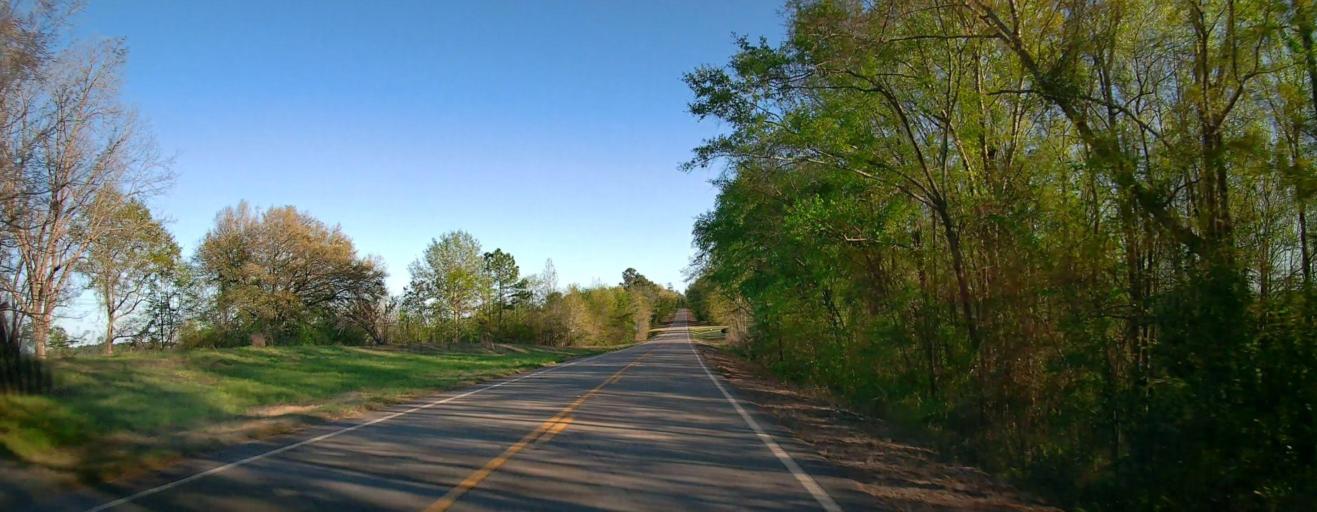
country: US
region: Georgia
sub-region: Wilkinson County
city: Irwinton
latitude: 32.8559
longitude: -83.0668
